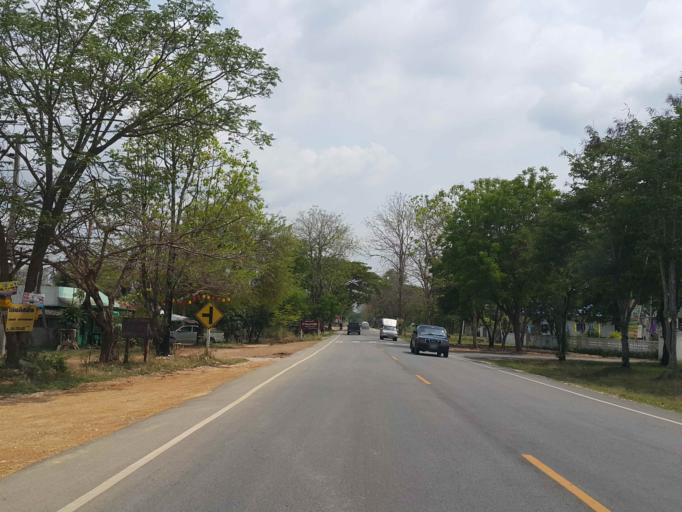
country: TH
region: Lampang
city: Thoen
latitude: 17.5130
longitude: 99.3506
